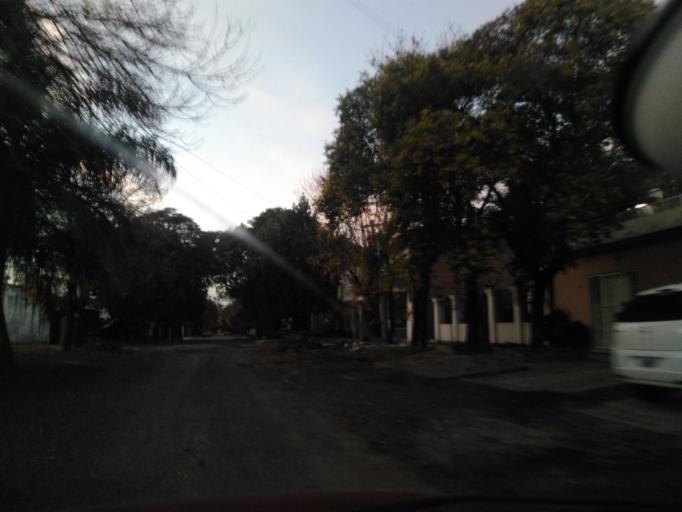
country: AR
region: Chaco
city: Resistencia
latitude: -27.4426
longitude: -58.9698
